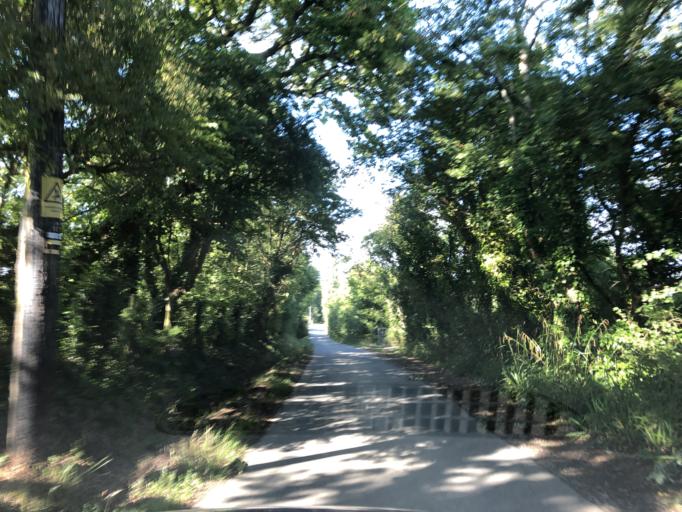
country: GB
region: England
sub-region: Isle of Wight
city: Shalfleet
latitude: 50.7038
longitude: -1.4422
